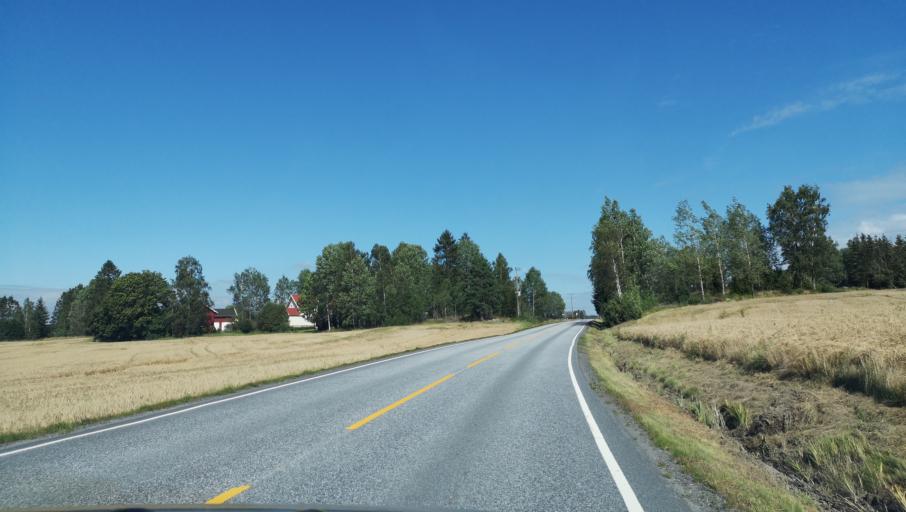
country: NO
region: Akershus
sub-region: Vestby
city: Vestby
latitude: 59.5443
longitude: 10.7881
